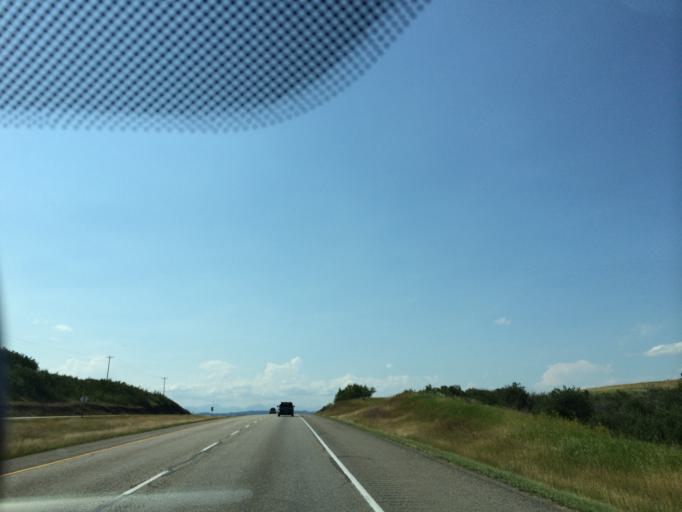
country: CA
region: Alberta
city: Cochrane
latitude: 51.0971
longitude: -114.5959
